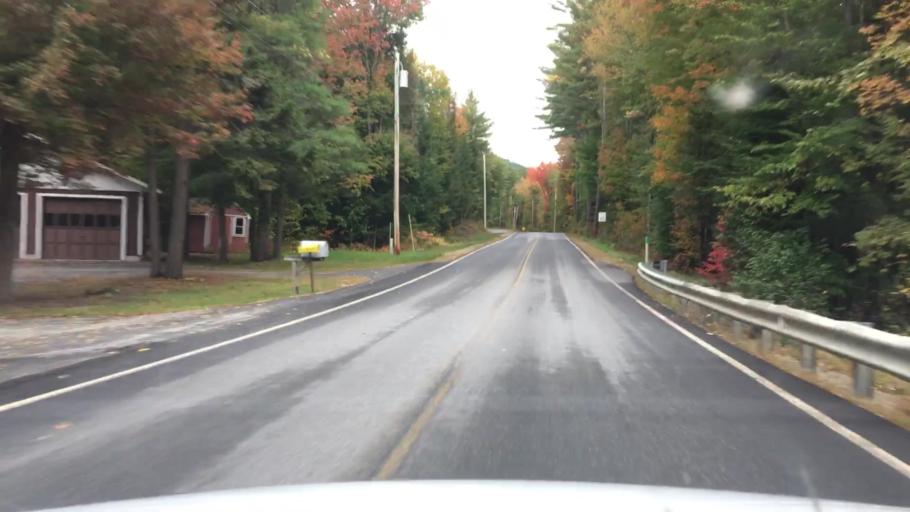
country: US
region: Maine
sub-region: Oxford County
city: Bethel
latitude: 44.2709
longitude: -70.7290
